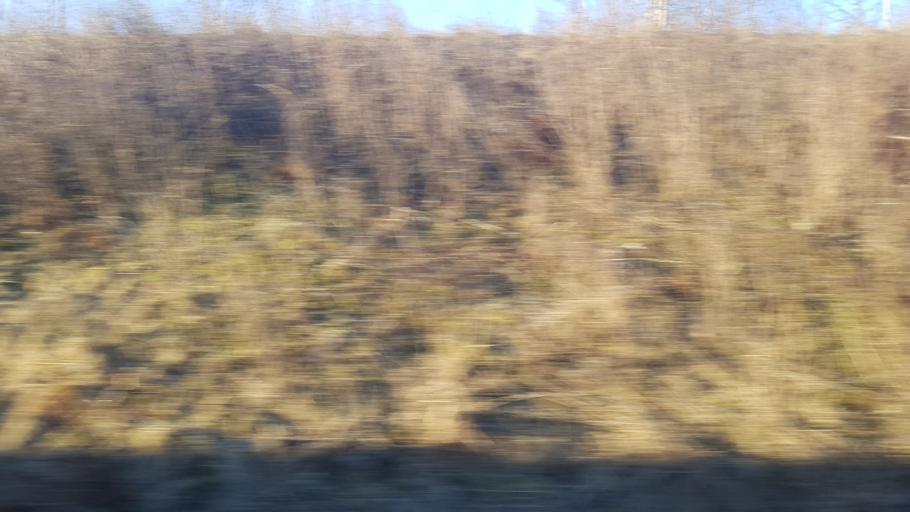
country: NO
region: Sor-Trondelag
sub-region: Malvik
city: Malvik
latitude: 63.4335
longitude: 10.6788
